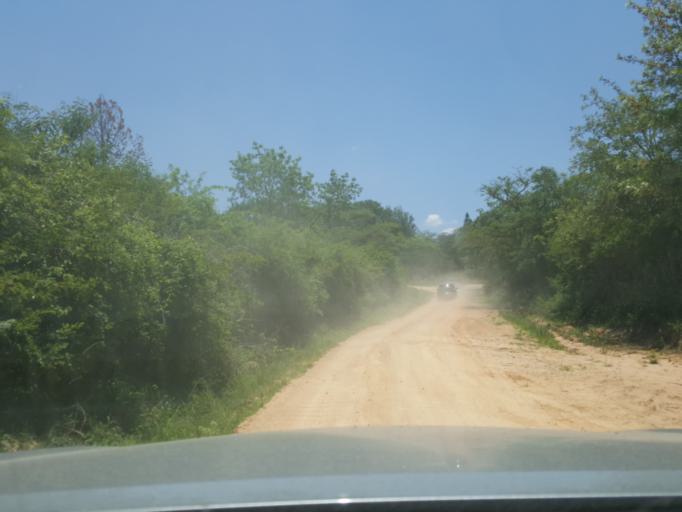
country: ZA
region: Limpopo
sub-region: Mopani District Municipality
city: Hoedspruit
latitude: -24.5917
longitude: 30.9439
